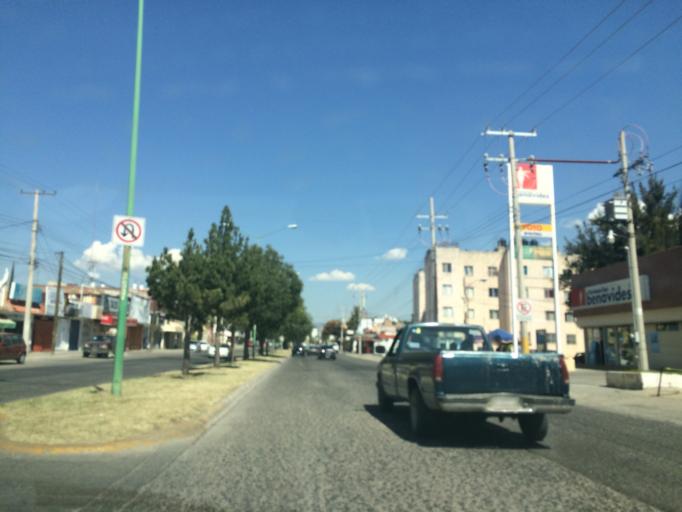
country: MX
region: Guanajuato
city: Leon
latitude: 21.0979
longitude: -101.6468
